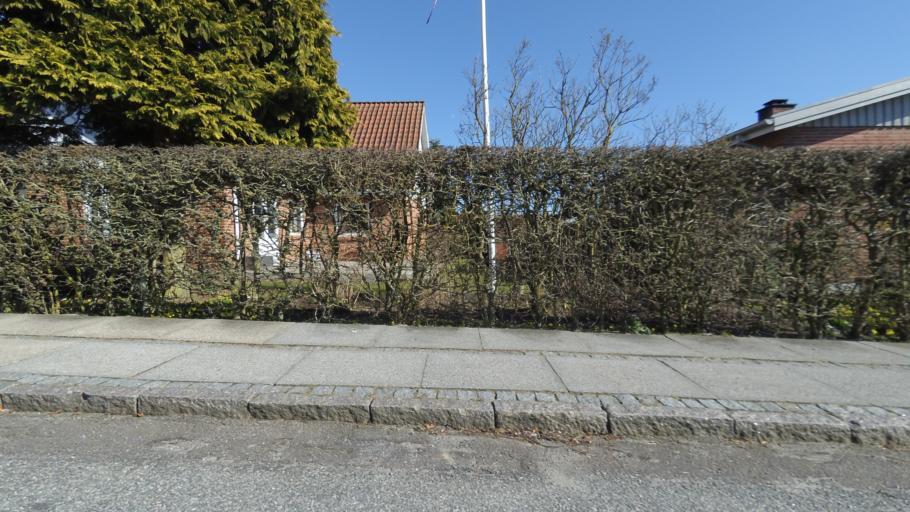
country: DK
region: Central Jutland
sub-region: Arhus Kommune
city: Arhus
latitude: 56.1690
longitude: 10.1689
